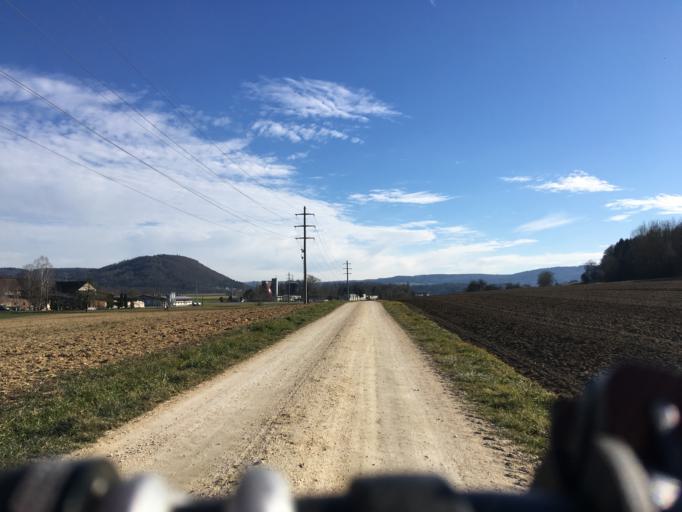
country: CH
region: Schaffhausen
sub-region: Bezirk Stein
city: Ramsen
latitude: 47.6981
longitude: 8.8104
